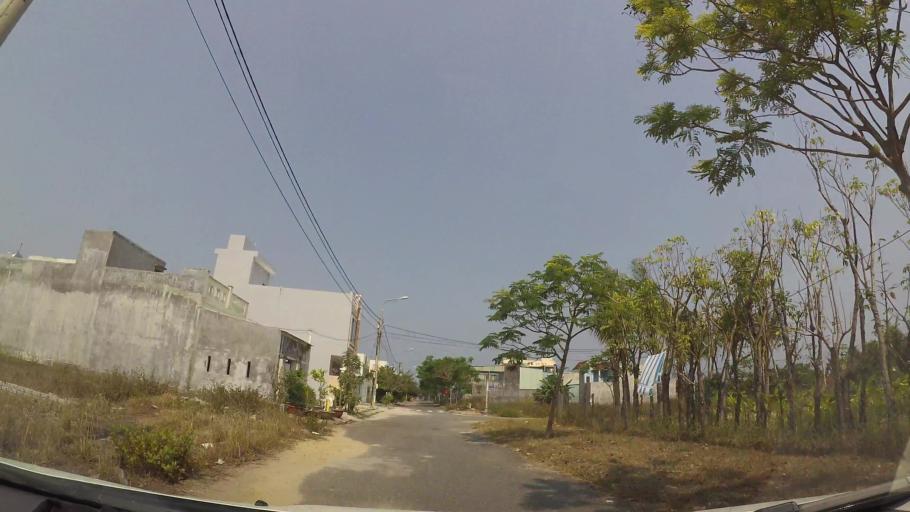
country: VN
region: Da Nang
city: Ngu Hanh Son
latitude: 15.9790
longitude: 108.2696
